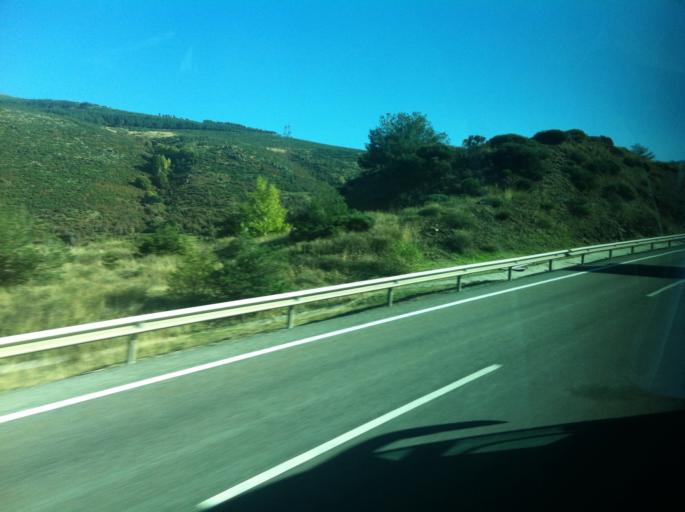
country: ES
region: Madrid
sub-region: Provincia de Madrid
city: Somosierra
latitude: 41.1425
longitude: -3.5819
